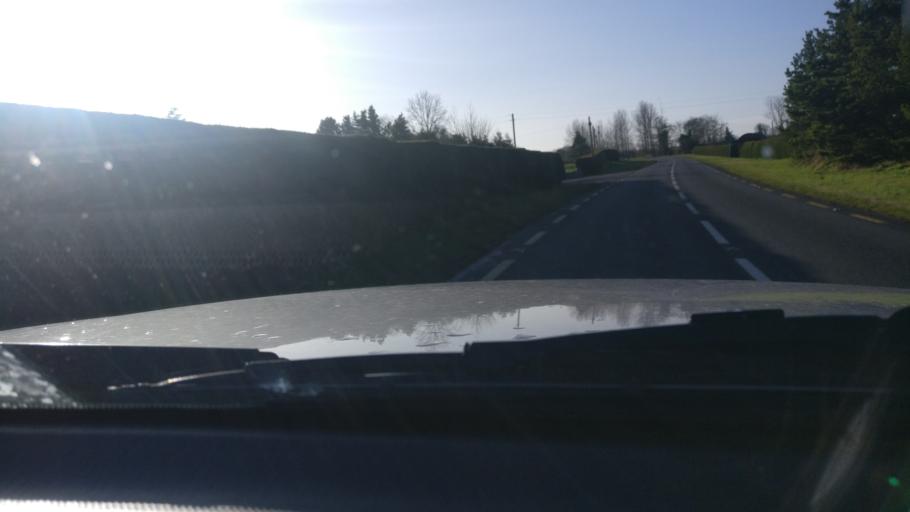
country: IE
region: Leinster
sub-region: An Longfort
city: Edgeworthstown
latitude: 53.6821
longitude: -7.6313
